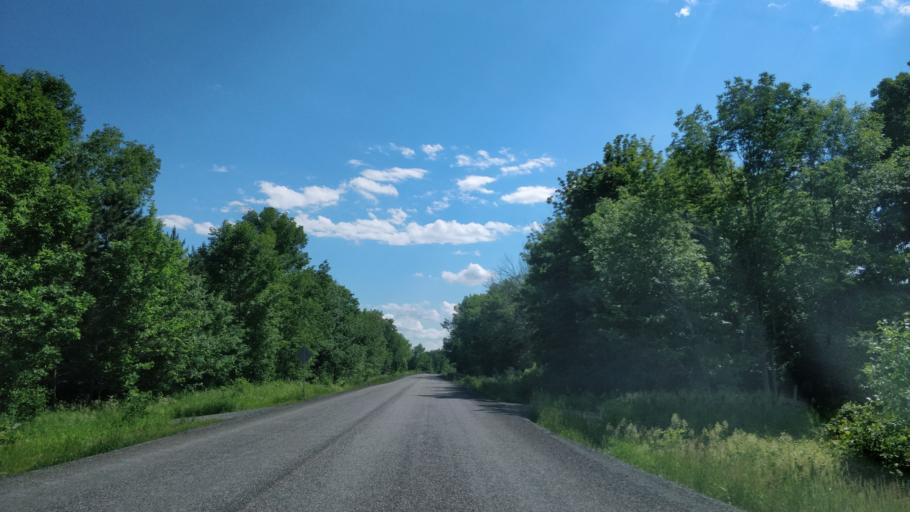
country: CA
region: Ontario
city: Perth
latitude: 44.7645
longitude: -76.4641
